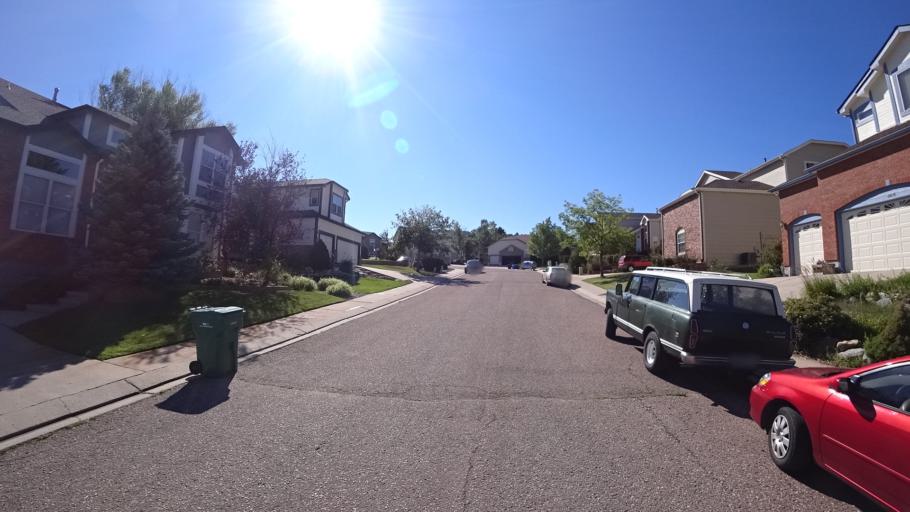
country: US
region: Colorado
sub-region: El Paso County
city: Gleneagle
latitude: 38.9804
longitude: -104.7787
